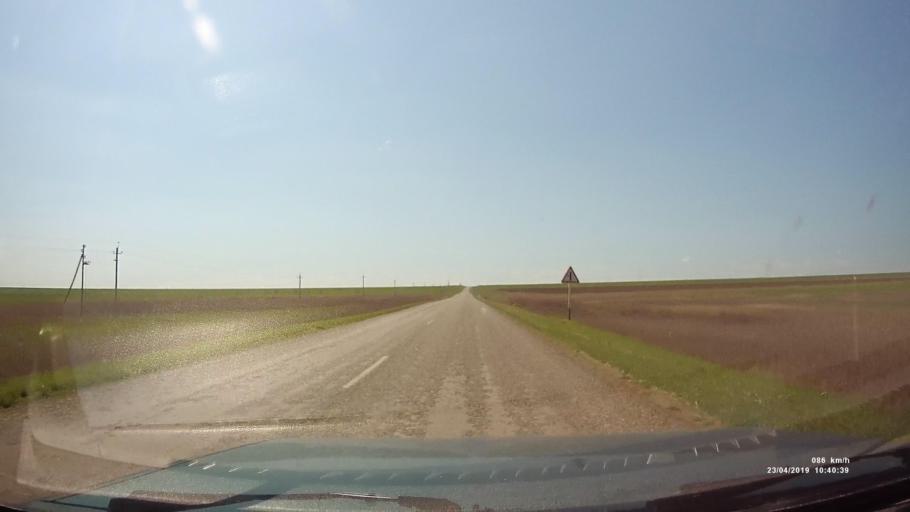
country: RU
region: Kalmykiya
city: Yashalta
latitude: 46.5038
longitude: 42.6384
